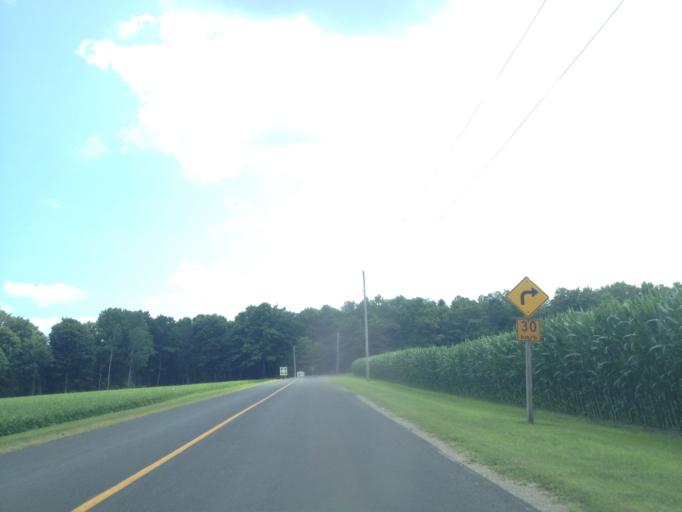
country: CA
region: Ontario
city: Aylmer
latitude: 42.6787
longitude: -81.0181
